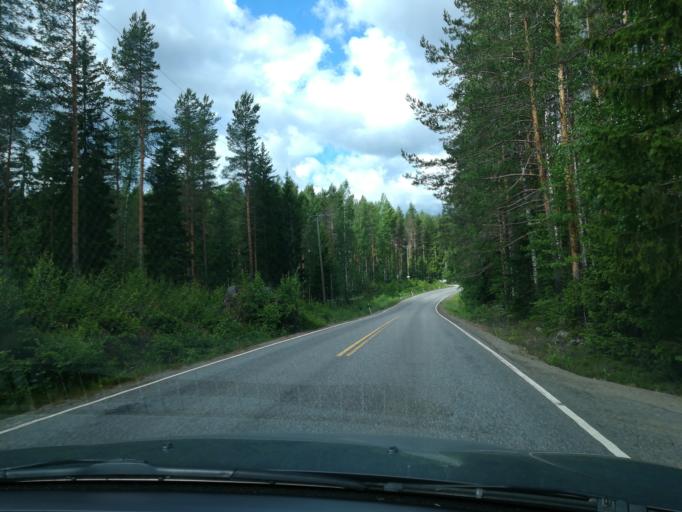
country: FI
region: Southern Savonia
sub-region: Mikkeli
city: Ristiina
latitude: 61.3503
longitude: 27.1347
